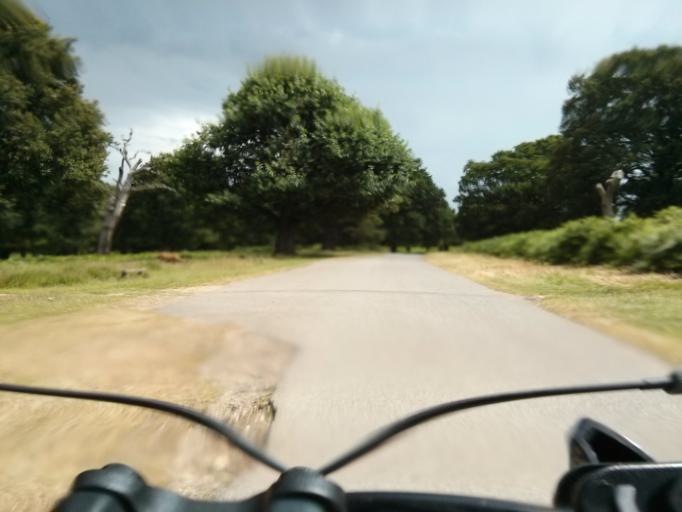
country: GB
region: England
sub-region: Greater London
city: Richmond
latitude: 51.4387
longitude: -0.2746
